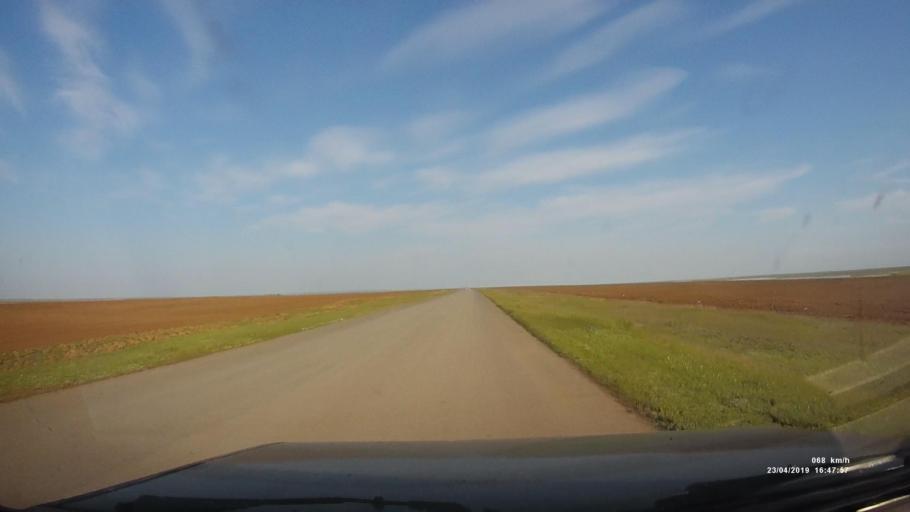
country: RU
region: Kalmykiya
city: Priyutnoye
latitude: 46.3368
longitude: 43.2549
